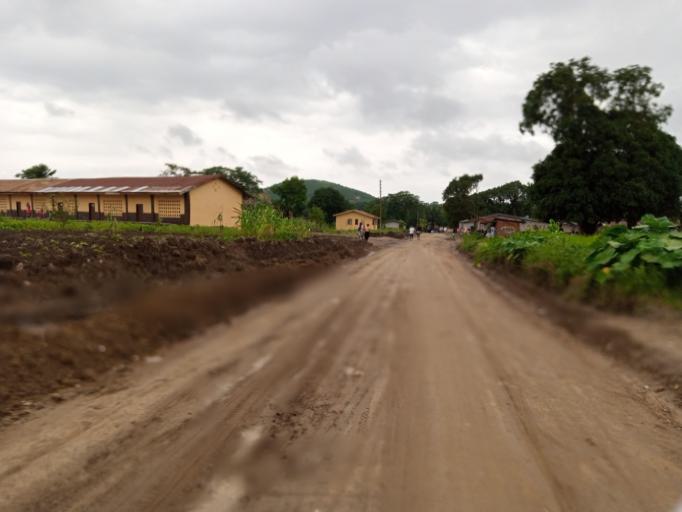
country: SL
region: Eastern Province
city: Kenema
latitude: 7.8599
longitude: -11.1986
